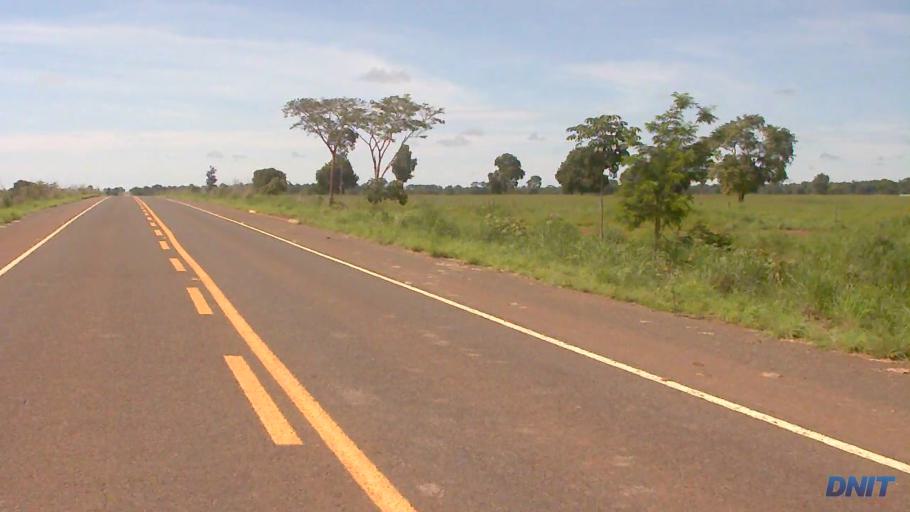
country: BR
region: Goias
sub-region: Sao Miguel Do Araguaia
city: Sao Miguel do Araguaia
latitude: -13.3817
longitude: -50.1405
